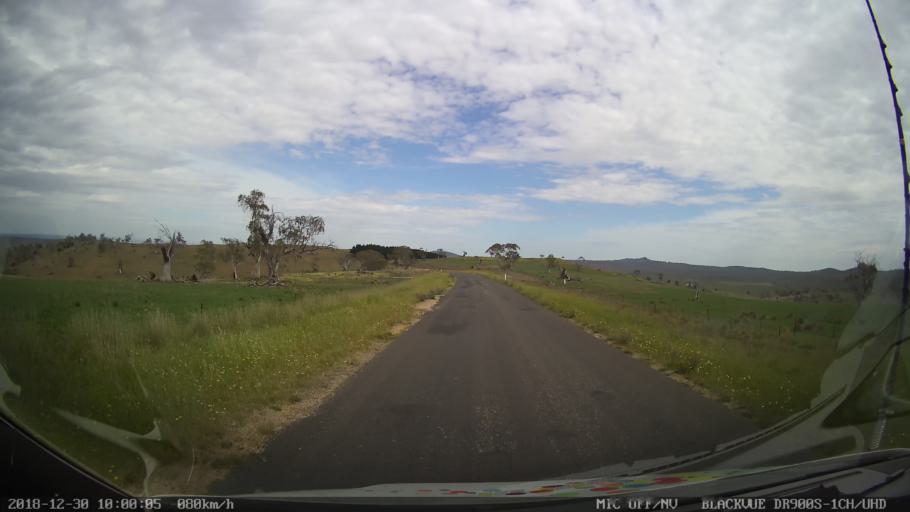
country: AU
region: New South Wales
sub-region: Cooma-Monaro
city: Cooma
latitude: -36.5189
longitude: 149.2024
